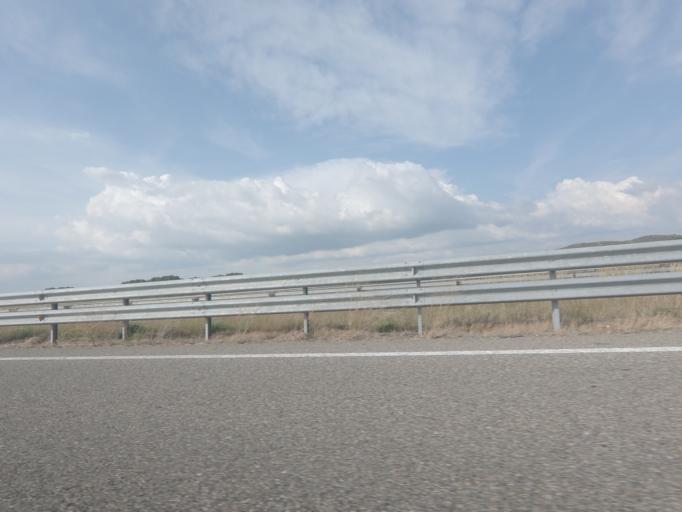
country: ES
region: Galicia
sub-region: Provincia de Ourense
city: Xinzo de Limia
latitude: 42.0805
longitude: -7.7130
